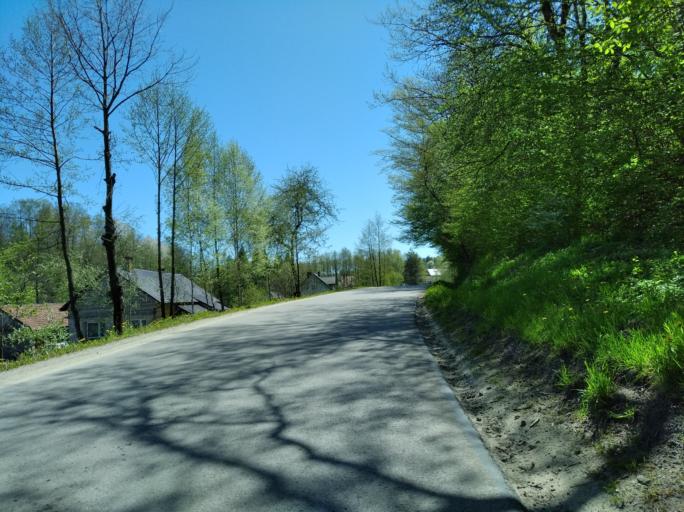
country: PL
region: Subcarpathian Voivodeship
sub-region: Powiat debicki
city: Brzostek
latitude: 49.9034
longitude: 21.4825
